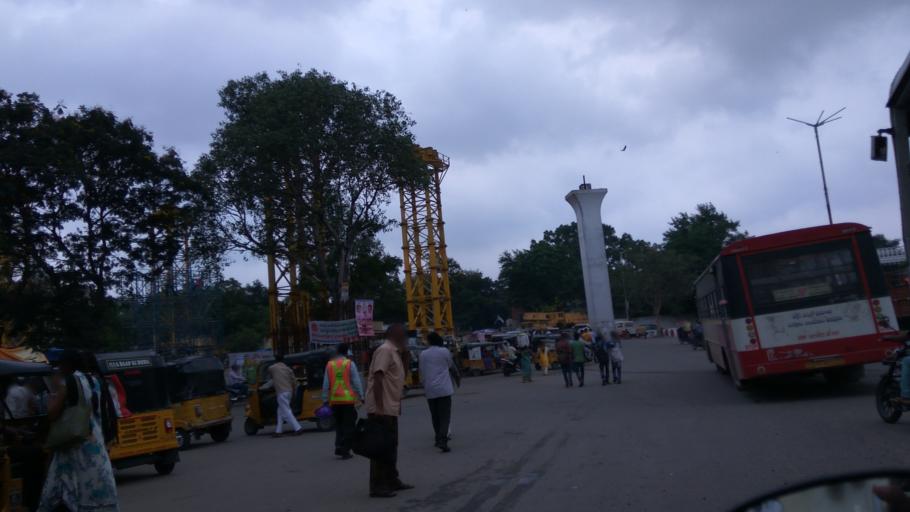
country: IN
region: Telangana
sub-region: Hyderabad
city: Malkajgiri
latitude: 17.4331
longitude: 78.5067
